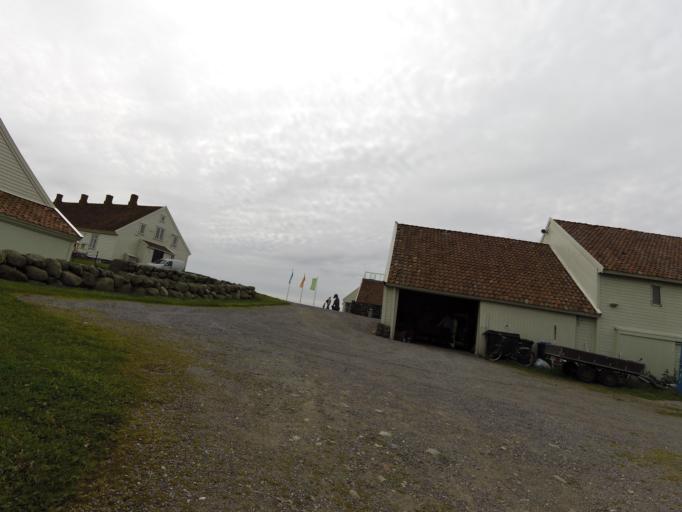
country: NO
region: Rogaland
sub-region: Ha
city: Naerbo
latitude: 58.6673
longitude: 5.5516
